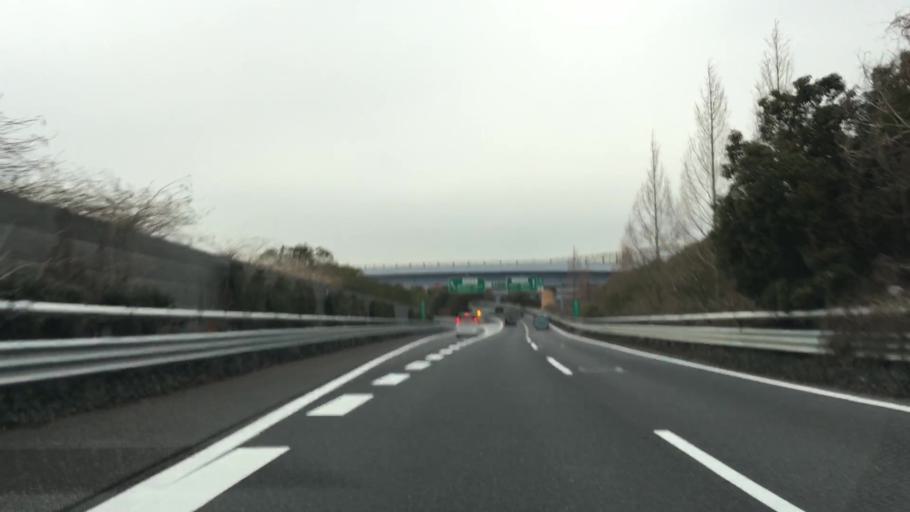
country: JP
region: Aichi
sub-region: Toyota-shi
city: Toyota
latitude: 35.0189
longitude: 137.1505
